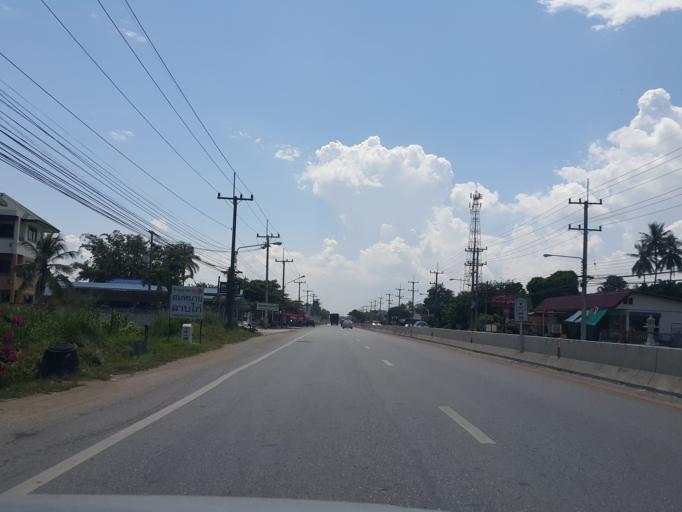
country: TH
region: Chiang Mai
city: Mae Taeng
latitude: 19.0172
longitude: 98.9445
